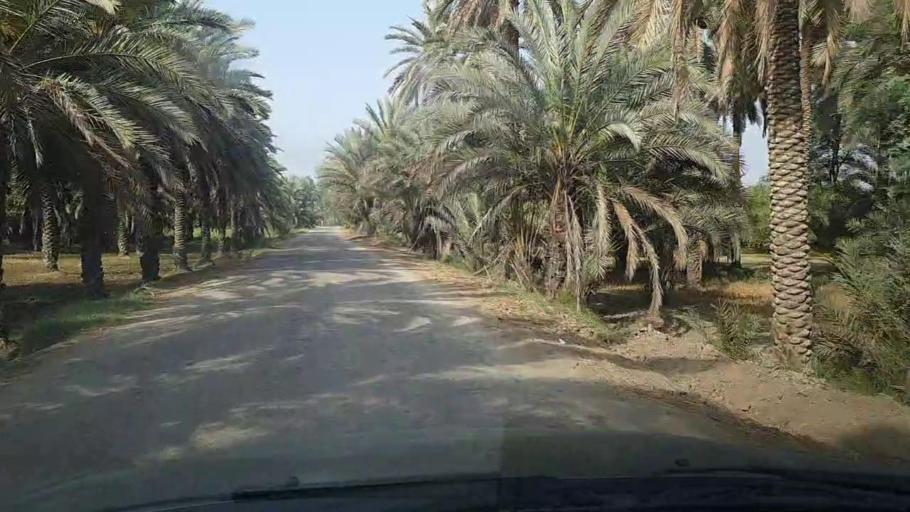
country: PK
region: Sindh
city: Pir jo Goth
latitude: 27.5526
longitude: 68.5341
